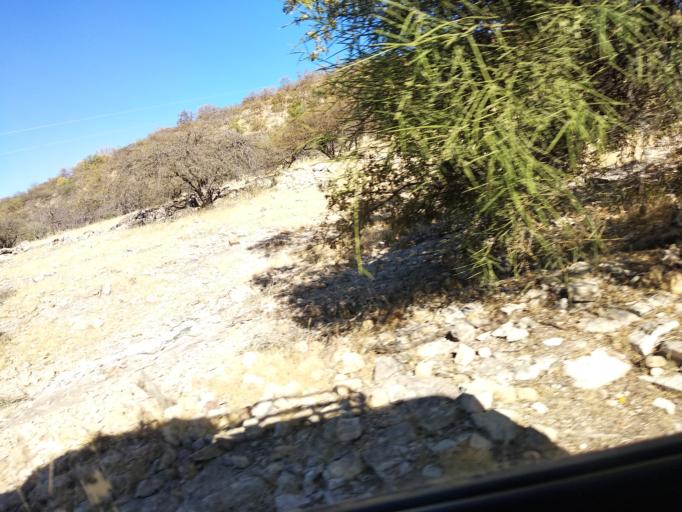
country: BO
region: Cochabamba
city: Mizque
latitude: -18.0838
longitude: -65.7512
